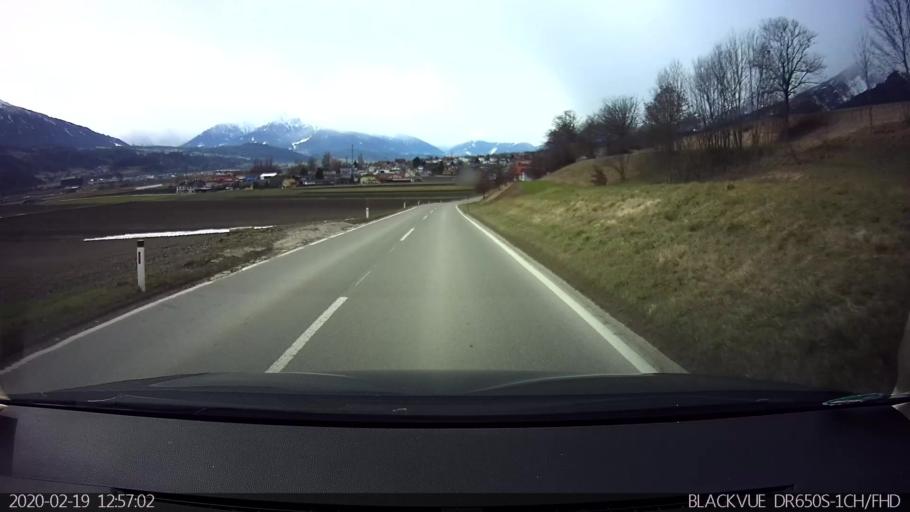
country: AT
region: Tyrol
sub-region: Politischer Bezirk Innsbruck Land
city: Absam
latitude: 47.2948
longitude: 11.4887
